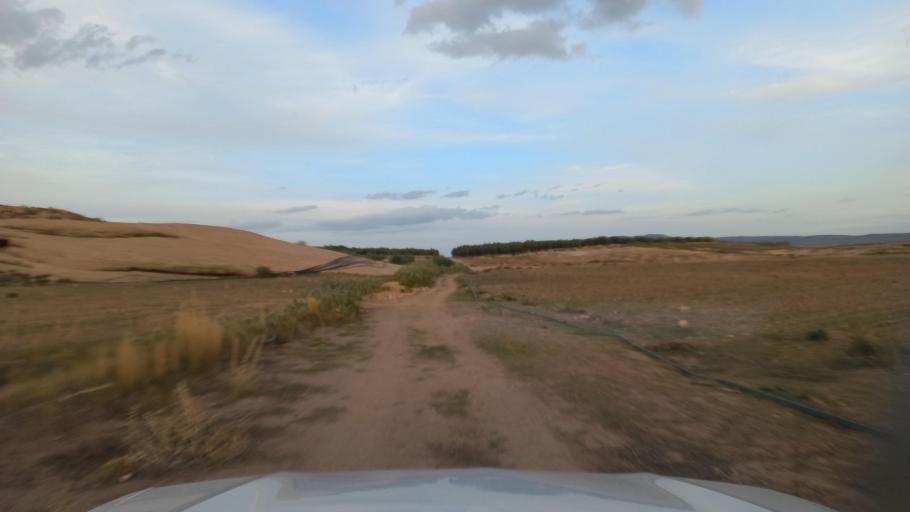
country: TN
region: Al Qasrayn
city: Sbiba
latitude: 35.4101
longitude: 9.0924
